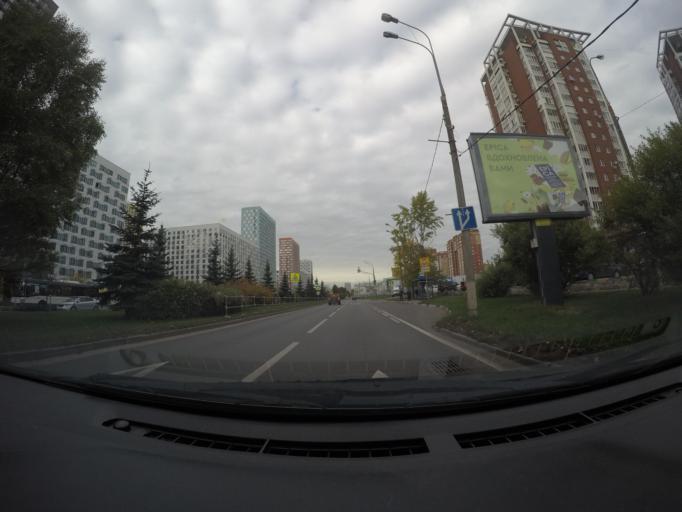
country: RU
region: Moskovskaya
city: Mytishchi
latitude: 55.9179
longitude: 37.7240
